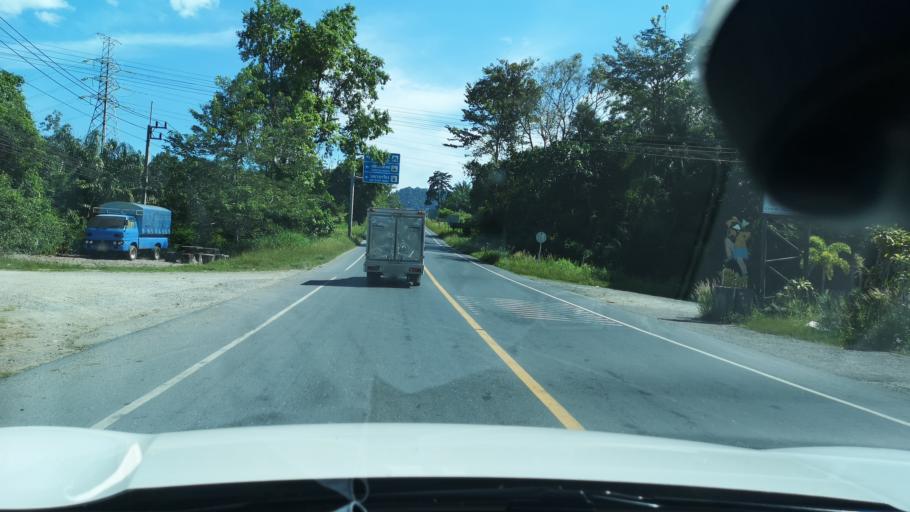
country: TH
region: Phangnga
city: Phang Nga
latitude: 8.5287
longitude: 98.5174
